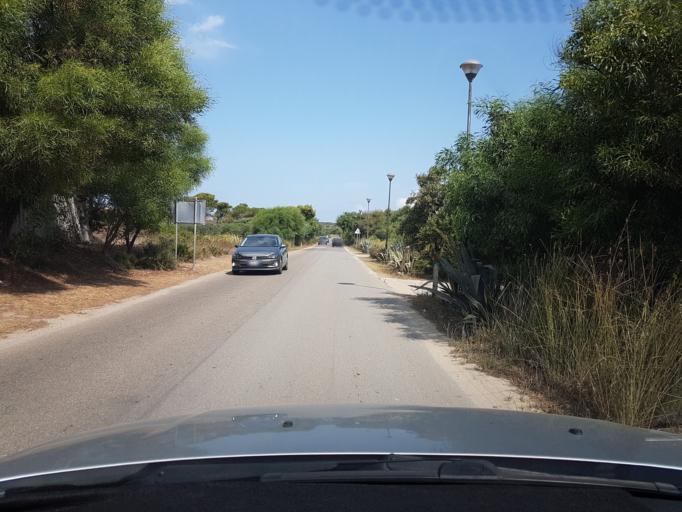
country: IT
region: Sardinia
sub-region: Provincia di Oristano
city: Cabras
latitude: 39.8848
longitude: 8.4376
